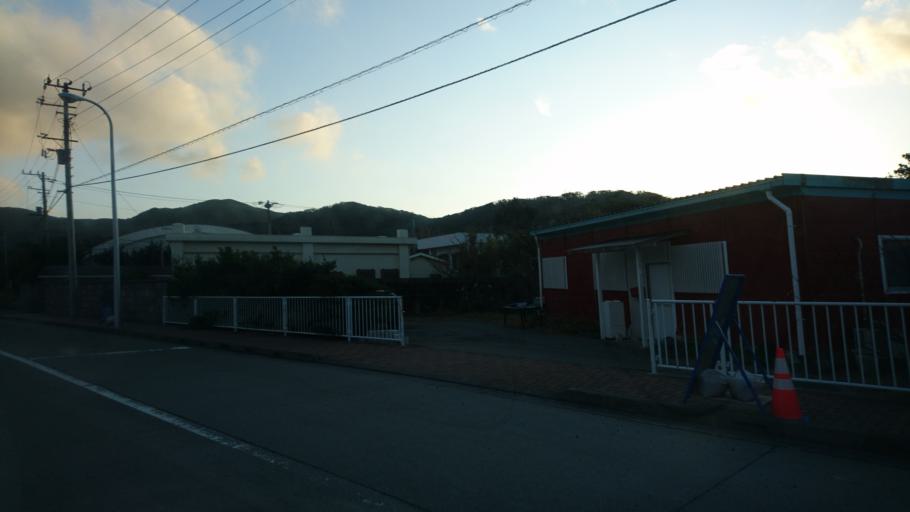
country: JP
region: Shizuoka
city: Shimoda
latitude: 34.3726
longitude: 139.2588
